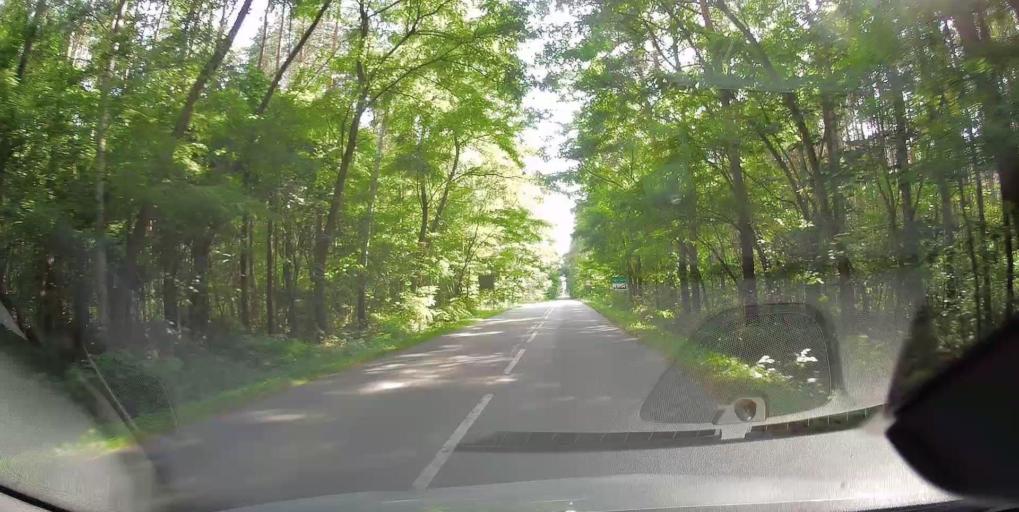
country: PL
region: Lodz Voivodeship
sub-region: Powiat opoczynski
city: Mniszkow
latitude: 51.4082
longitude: 20.0471
